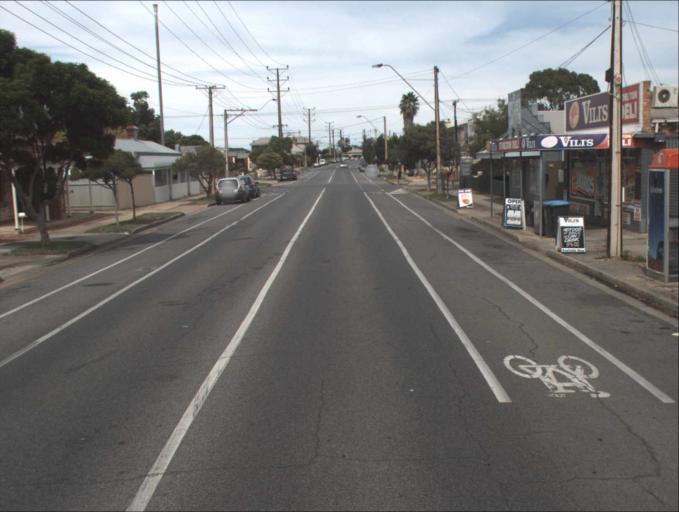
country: AU
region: South Australia
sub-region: Charles Sturt
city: West Lakes Shore
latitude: -34.8477
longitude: 138.4907
